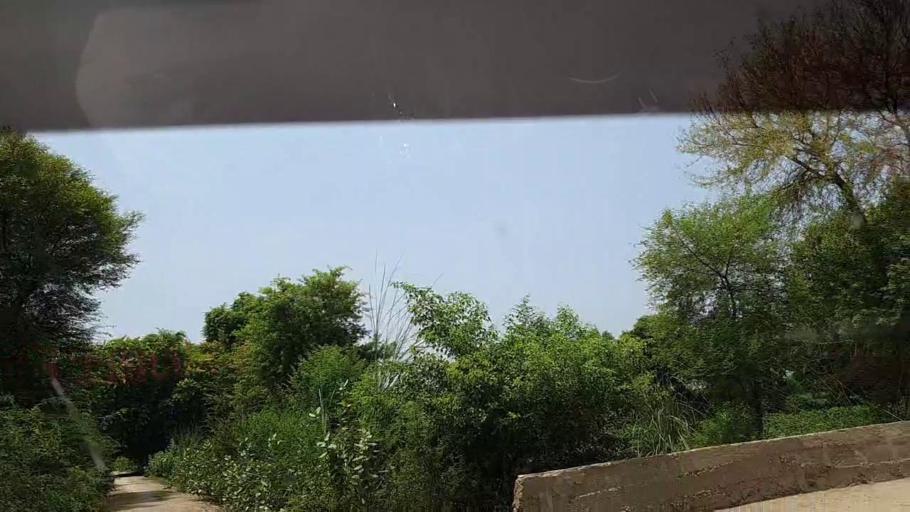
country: PK
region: Sindh
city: Adilpur
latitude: 27.8798
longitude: 69.2612
